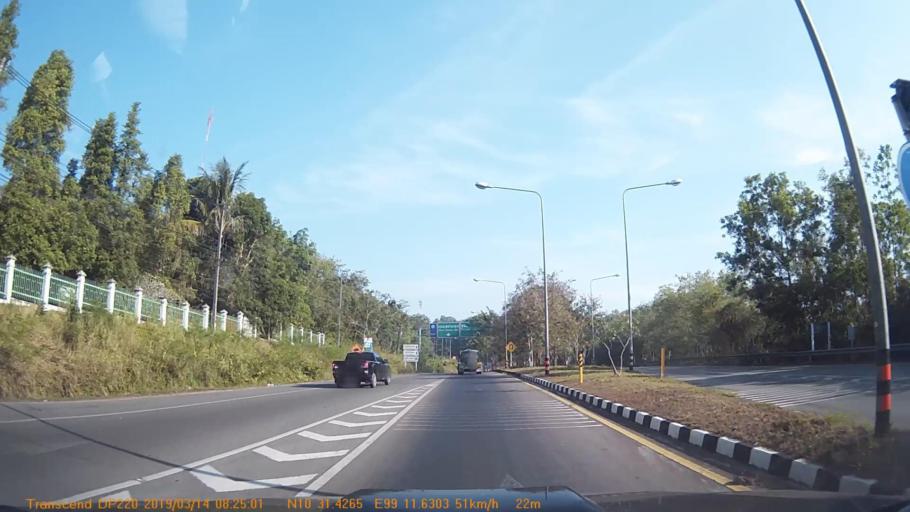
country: TH
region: Chumphon
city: Chumphon
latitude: 10.5239
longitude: 99.1938
